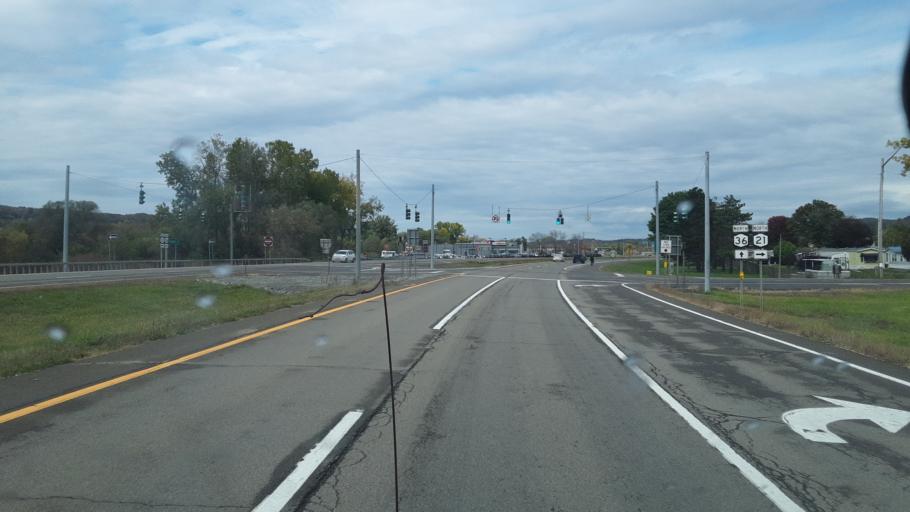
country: US
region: New York
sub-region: Steuben County
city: Hornell
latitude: 42.3621
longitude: -77.6723
